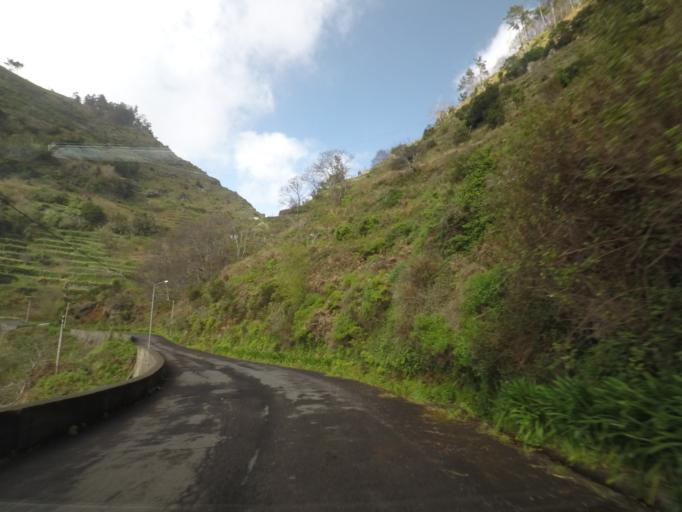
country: PT
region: Madeira
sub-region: Ribeira Brava
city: Campanario
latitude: 32.7028
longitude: -17.0243
